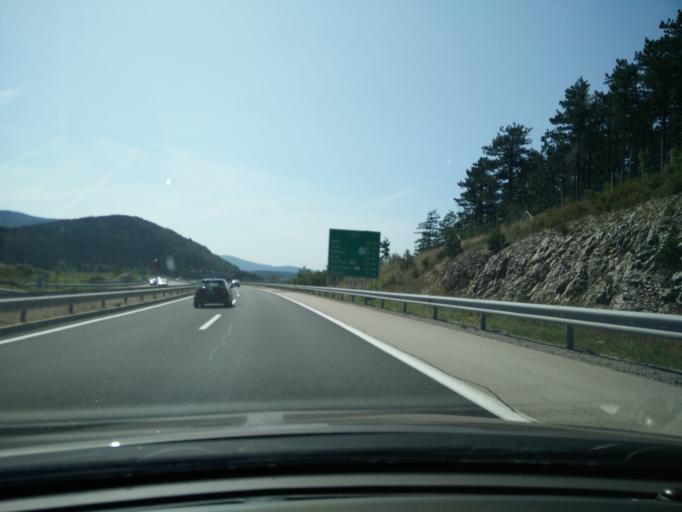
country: SI
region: Hrpelje-Kozina
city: Kozina
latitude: 45.6036
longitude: 13.9278
